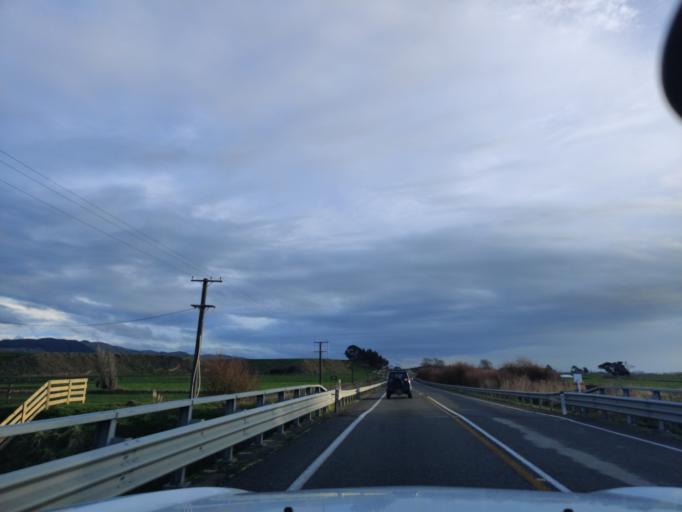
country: NZ
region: Manawatu-Wanganui
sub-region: Horowhenua District
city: Foxton
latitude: -40.5327
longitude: 175.4317
